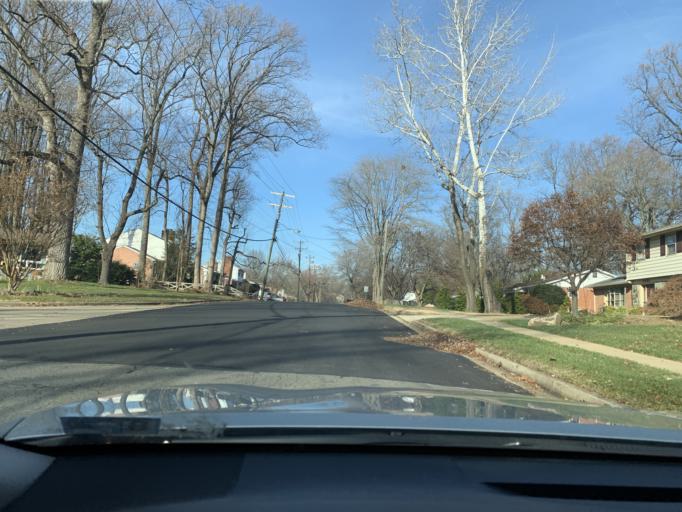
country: US
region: Virginia
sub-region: Fairfax County
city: Jefferson
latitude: 38.8509
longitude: -77.1853
